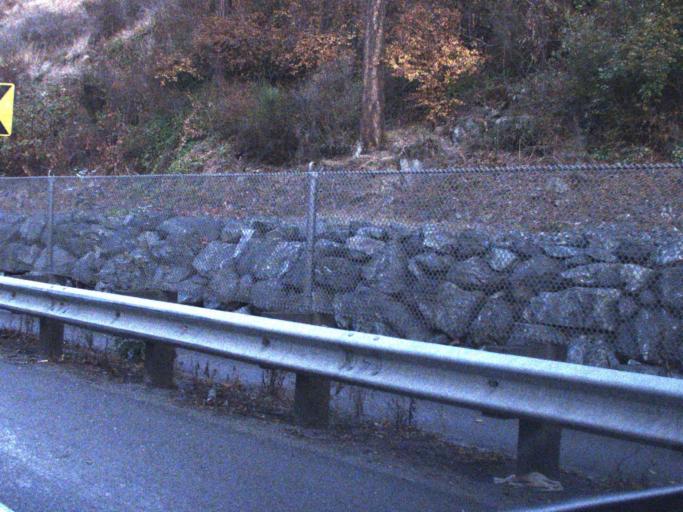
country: US
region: Washington
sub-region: Skagit County
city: Anacortes
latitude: 48.4426
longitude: -122.6016
